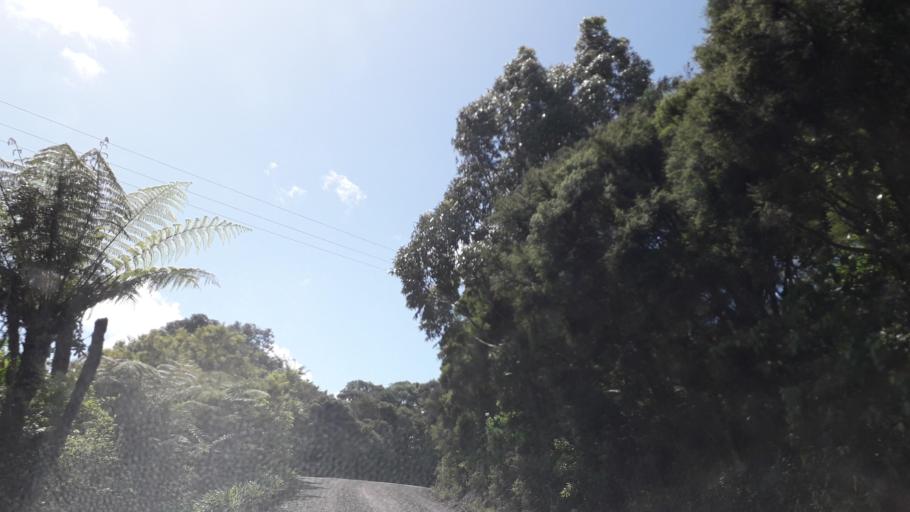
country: NZ
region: Northland
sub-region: Far North District
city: Paihia
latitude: -35.2385
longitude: 174.2555
